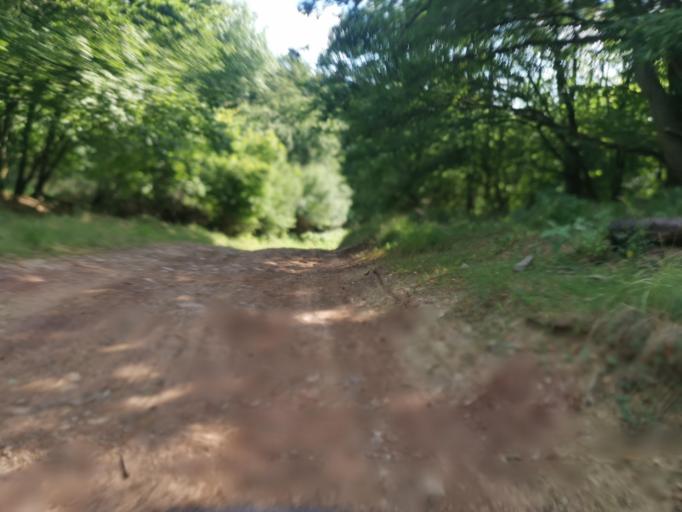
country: SK
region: Trnavsky
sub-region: Okres Senica
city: Senica
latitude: 48.7822
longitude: 17.3532
